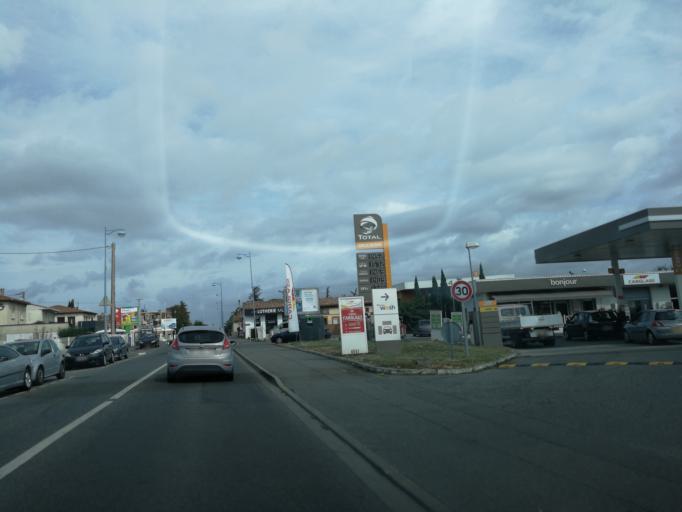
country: FR
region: Midi-Pyrenees
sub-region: Departement de la Haute-Garonne
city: Saint-Alban
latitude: 43.6832
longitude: 1.4203
